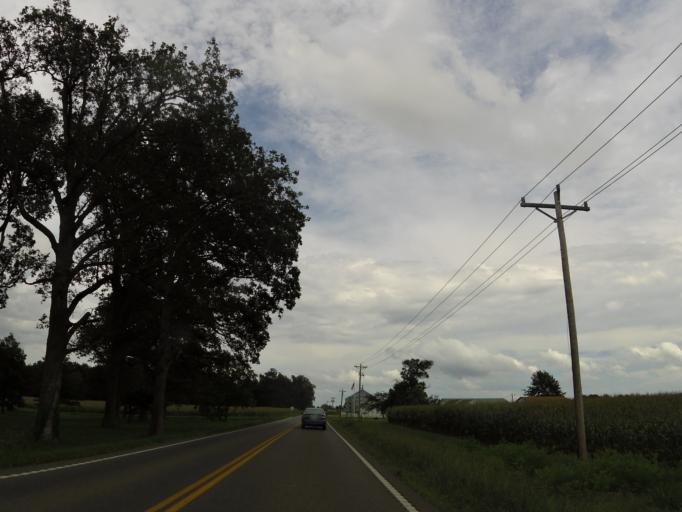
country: US
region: Kentucky
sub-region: Ballard County
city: La Center
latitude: 37.0051
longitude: -88.8632
